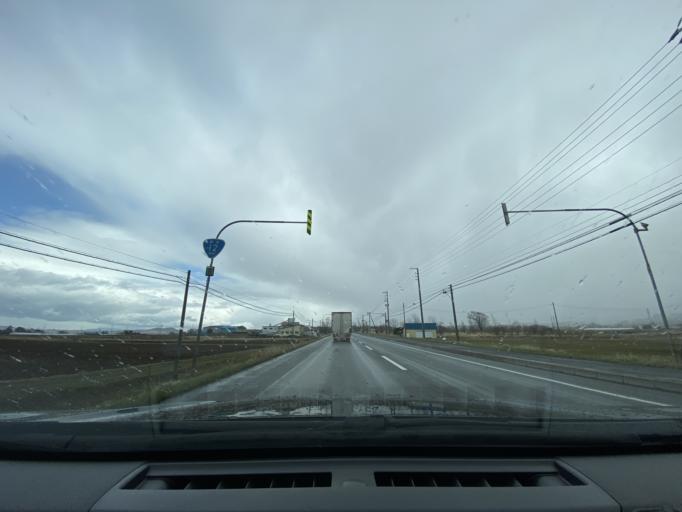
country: JP
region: Hokkaido
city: Fukagawa
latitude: 43.6823
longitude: 142.0411
